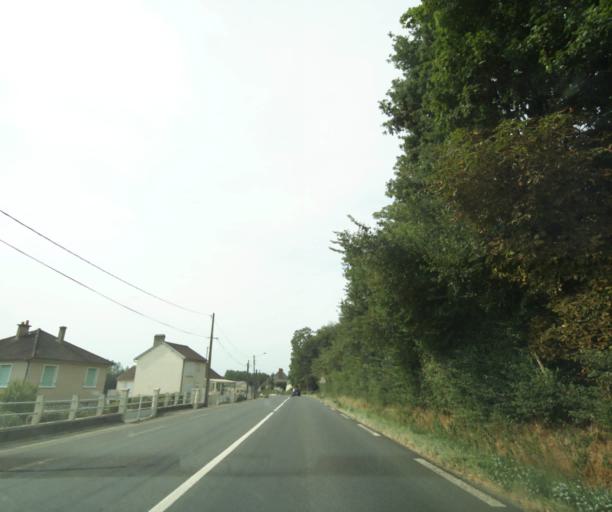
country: FR
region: Centre
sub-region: Departement d'Indre-et-Loire
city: Saint-Christophe-sur-le-Nais
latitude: 47.6617
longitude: 0.4763
